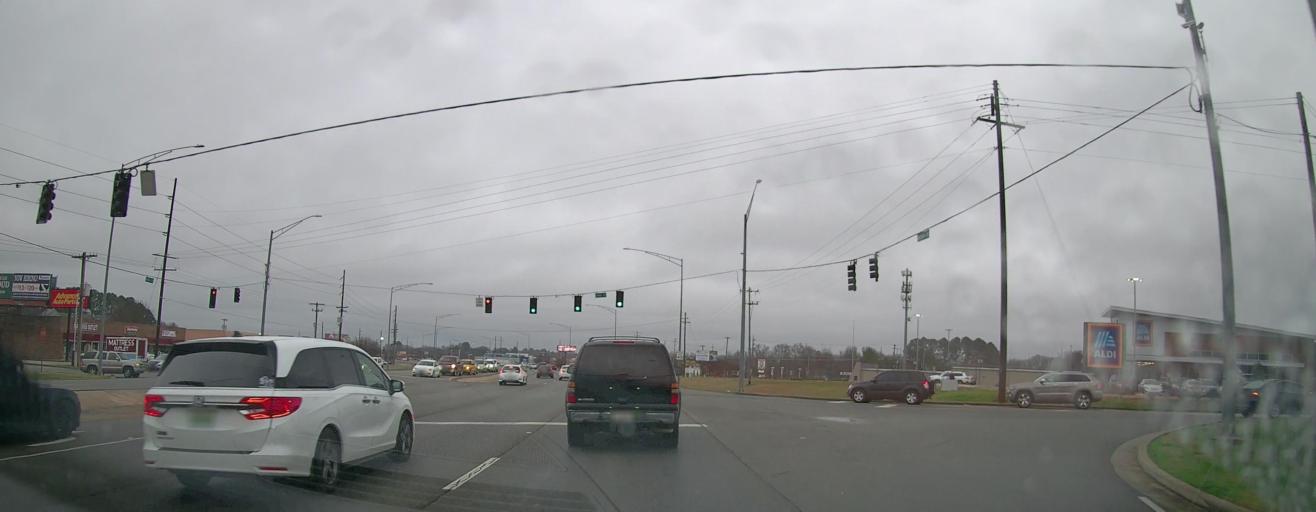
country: US
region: Alabama
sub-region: Morgan County
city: Decatur
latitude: 34.5644
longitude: -87.0100
